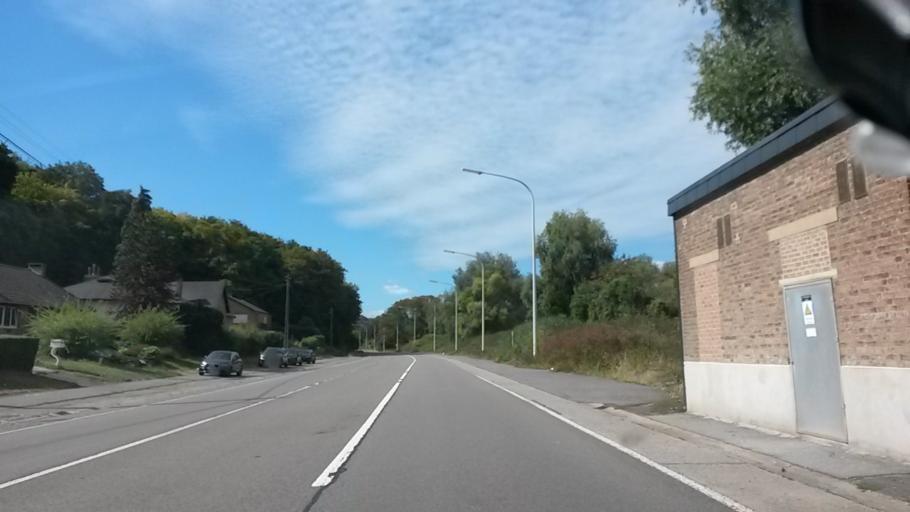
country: BE
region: Wallonia
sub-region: Province de Liege
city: Wanze
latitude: 50.5240
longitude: 5.2007
